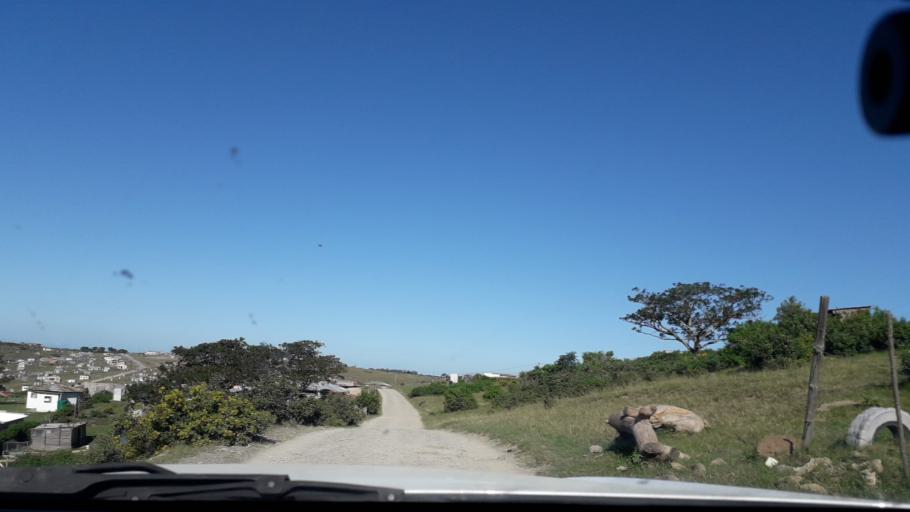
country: ZA
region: Eastern Cape
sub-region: Buffalo City Metropolitan Municipality
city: East London
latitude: -32.8443
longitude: 27.9892
